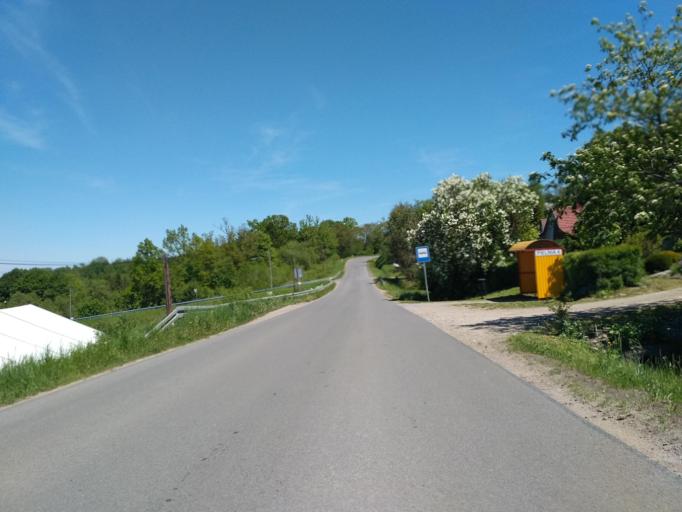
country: PL
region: Subcarpathian Voivodeship
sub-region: Powiat sanocki
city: Nowosielce-Gniewosz
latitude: 49.5381
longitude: 22.0574
